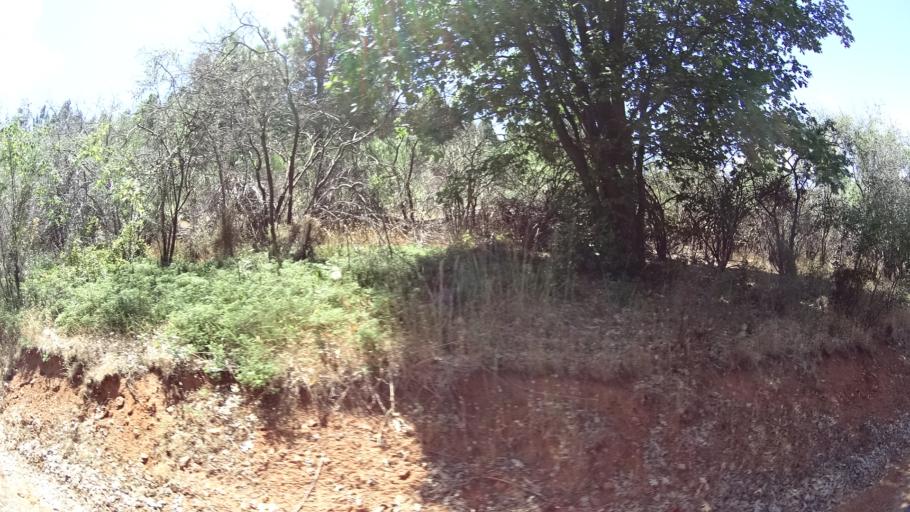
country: US
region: California
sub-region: Calaveras County
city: Forest Meadows
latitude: 38.1978
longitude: -120.4283
